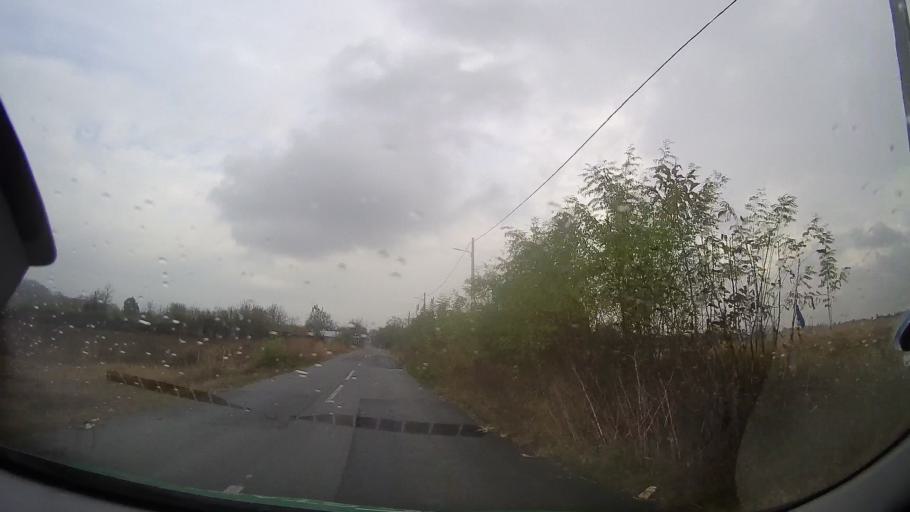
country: RO
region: Prahova
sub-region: Comuna Draganesti
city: Draganesti
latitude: 44.7858
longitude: 26.3169
